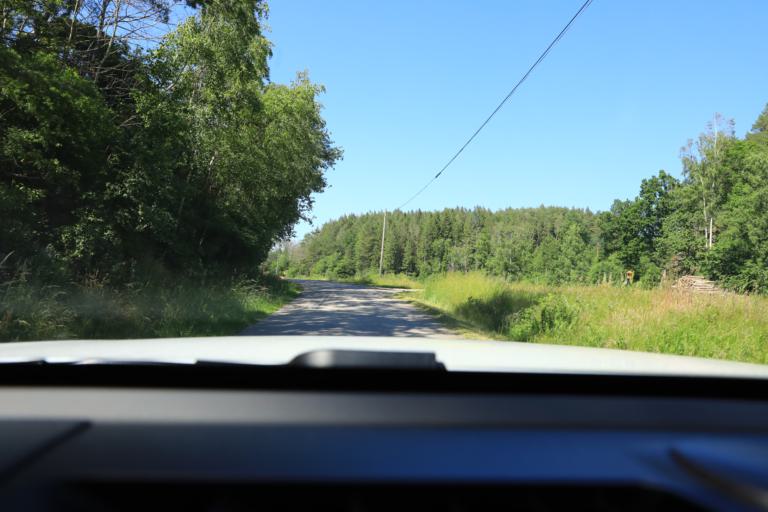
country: SE
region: Halland
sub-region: Varbergs Kommun
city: Veddige
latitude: 57.1915
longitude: 12.3237
